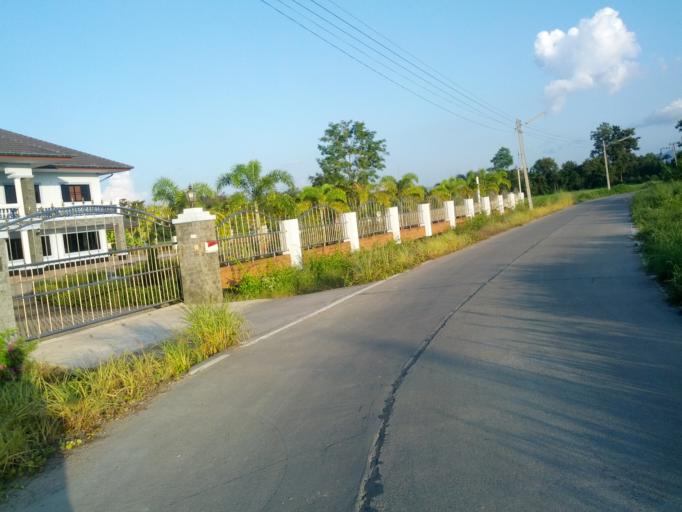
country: TH
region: Chiang Mai
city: San Kamphaeng
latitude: 18.7679
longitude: 99.0978
